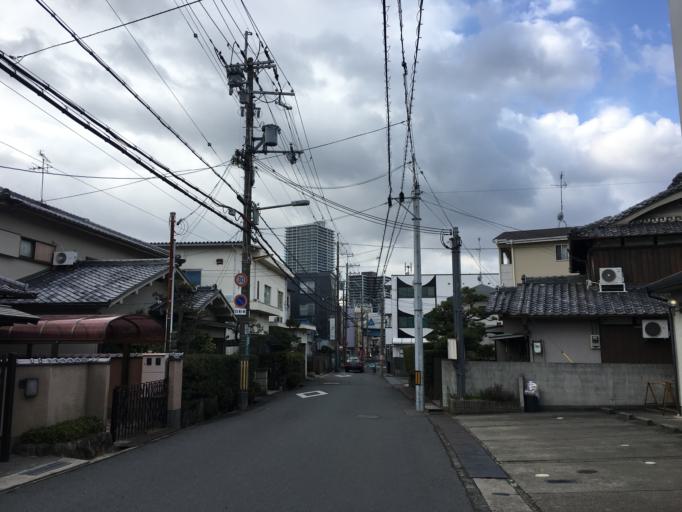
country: JP
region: Osaka
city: Takatsuki
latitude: 34.8573
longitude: 135.6269
